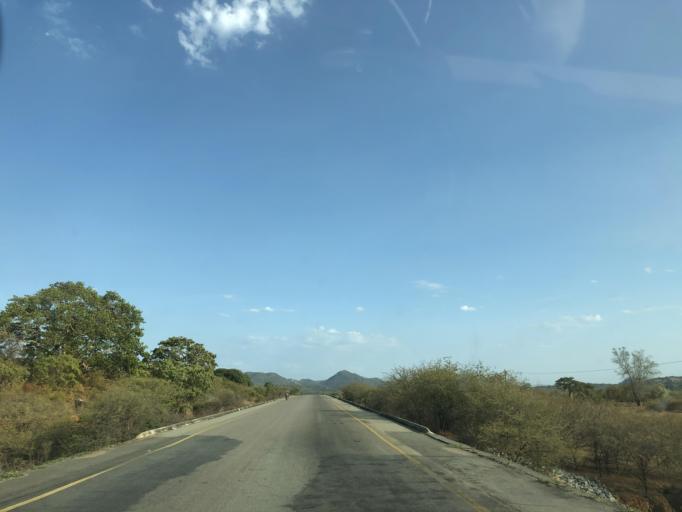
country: AO
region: Huila
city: Caluquembe
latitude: -13.3698
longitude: 13.8678
